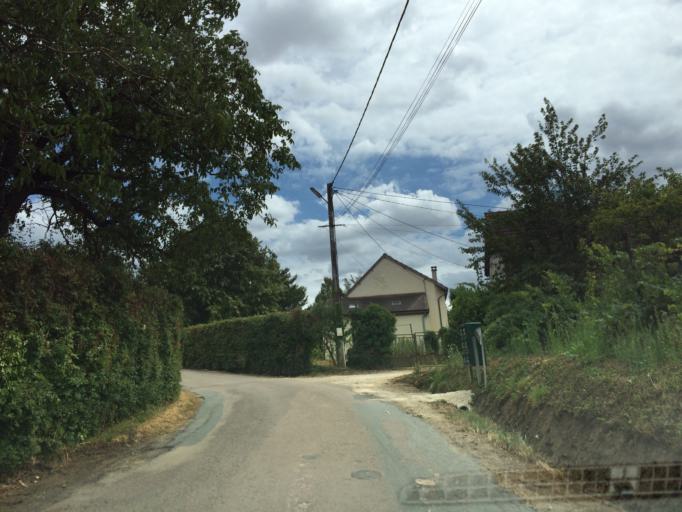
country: FR
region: Bourgogne
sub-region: Departement de l'Yonne
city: Fleury-la-Vallee
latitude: 47.8467
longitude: 3.4078
